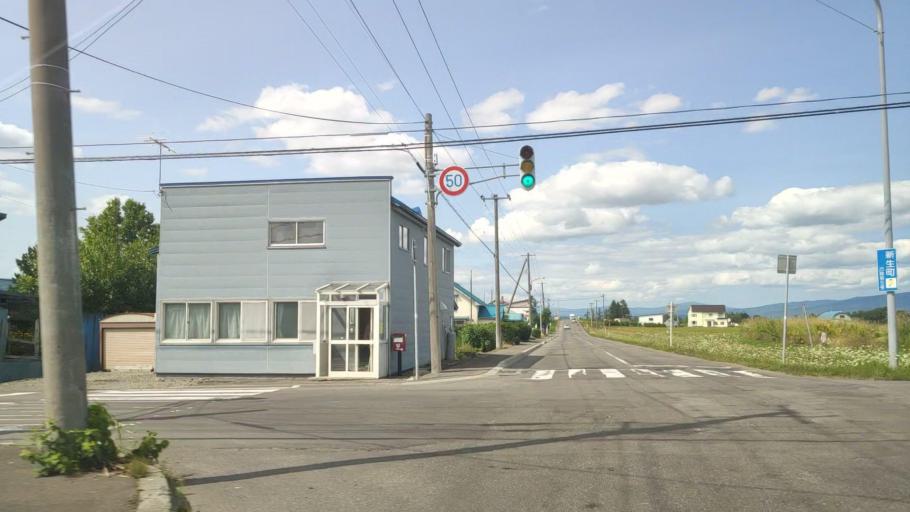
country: JP
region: Hokkaido
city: Nayoro
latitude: 44.2961
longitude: 142.4294
